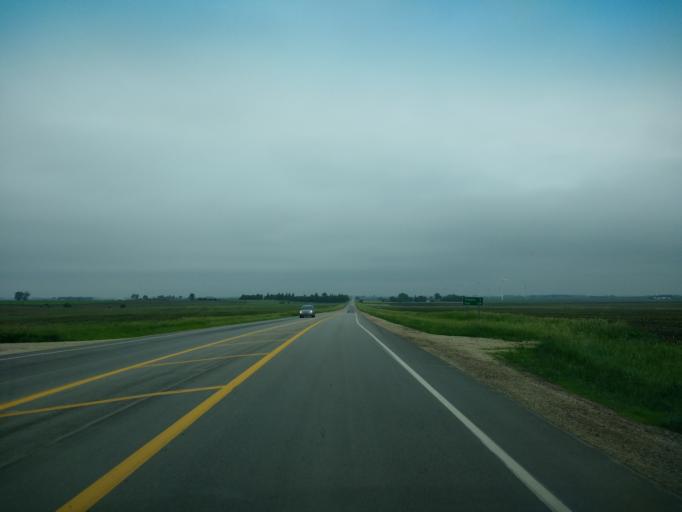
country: US
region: Iowa
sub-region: O'Brien County
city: Sanborn
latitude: 43.1861
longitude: -95.6649
